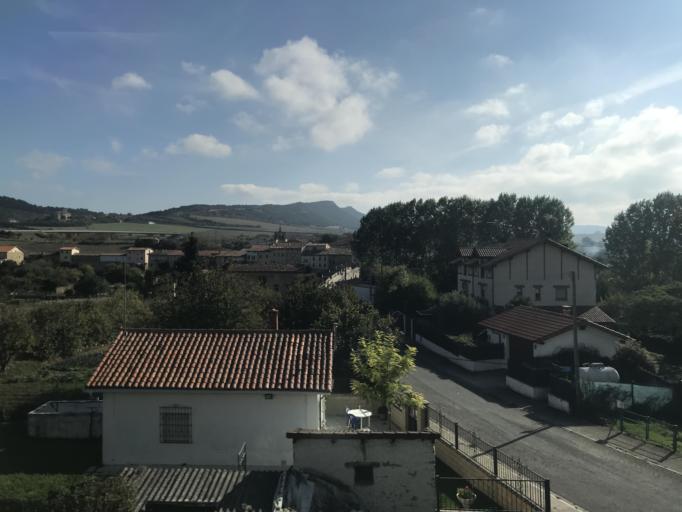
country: ES
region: Basque Country
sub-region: Provincia de Alava
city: Arminon
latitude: 42.7229
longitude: -2.8758
